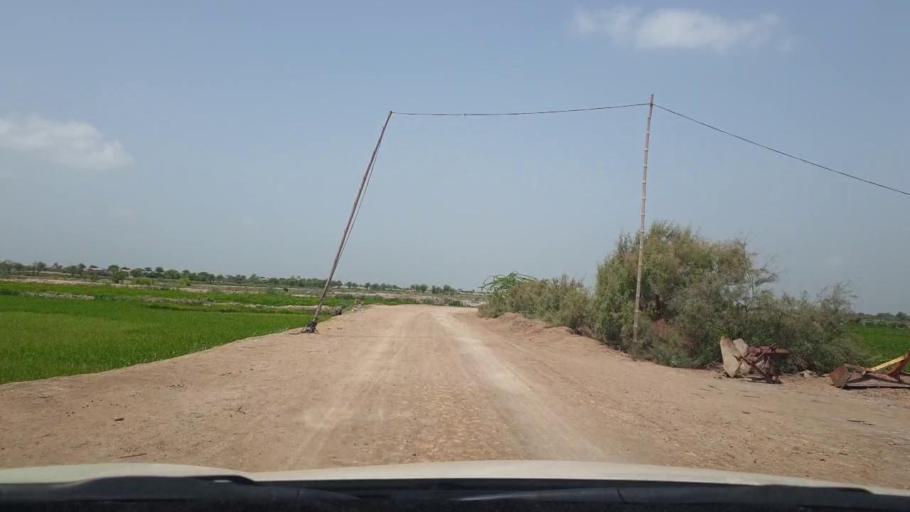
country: PK
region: Sindh
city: Talhar
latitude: 24.9245
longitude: 68.8346
